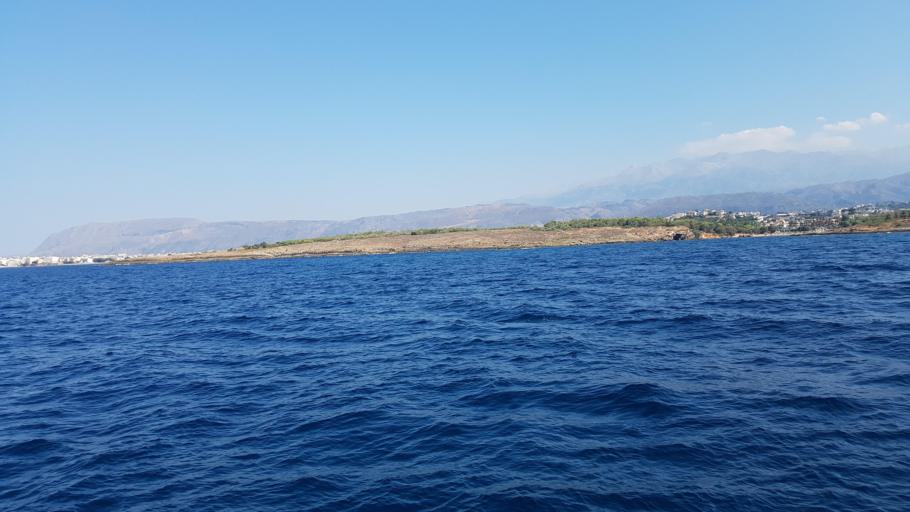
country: GR
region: Crete
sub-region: Nomos Chanias
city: Daratsos
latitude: 35.5217
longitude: 23.9822
